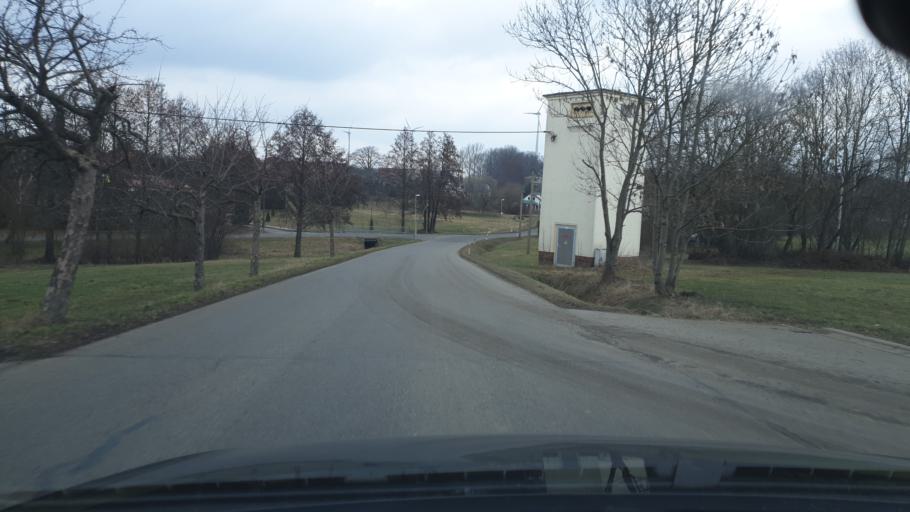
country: DE
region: Saxony
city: Erlau
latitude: 51.0043
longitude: 12.9206
